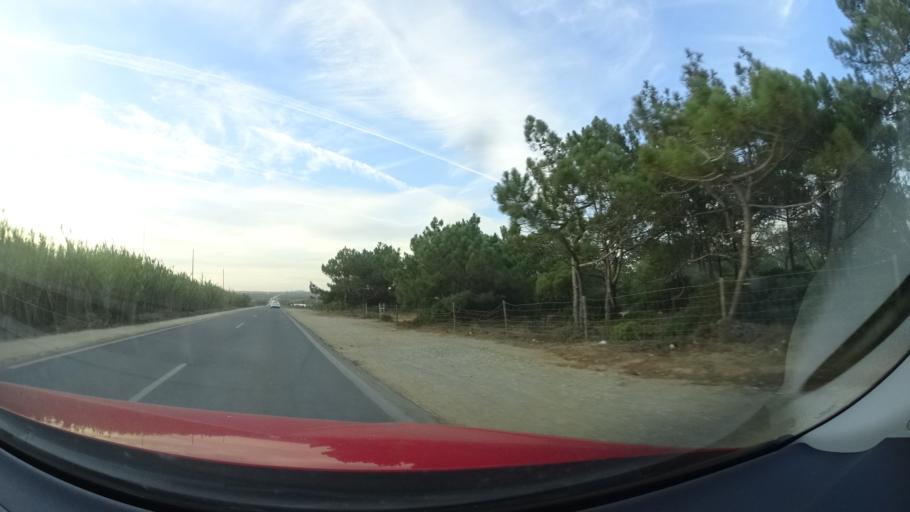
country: PT
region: Faro
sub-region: Vila do Bispo
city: Sagres
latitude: 37.0100
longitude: -8.9493
